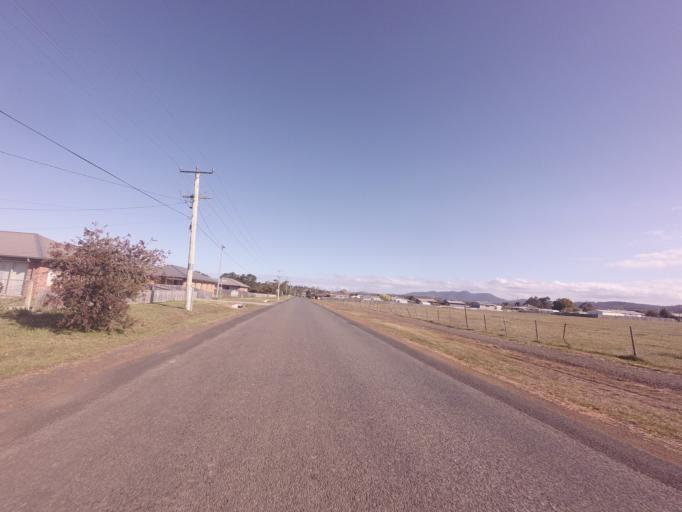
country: AU
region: Tasmania
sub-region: Sorell
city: Sorell
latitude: -42.5040
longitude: 147.9156
